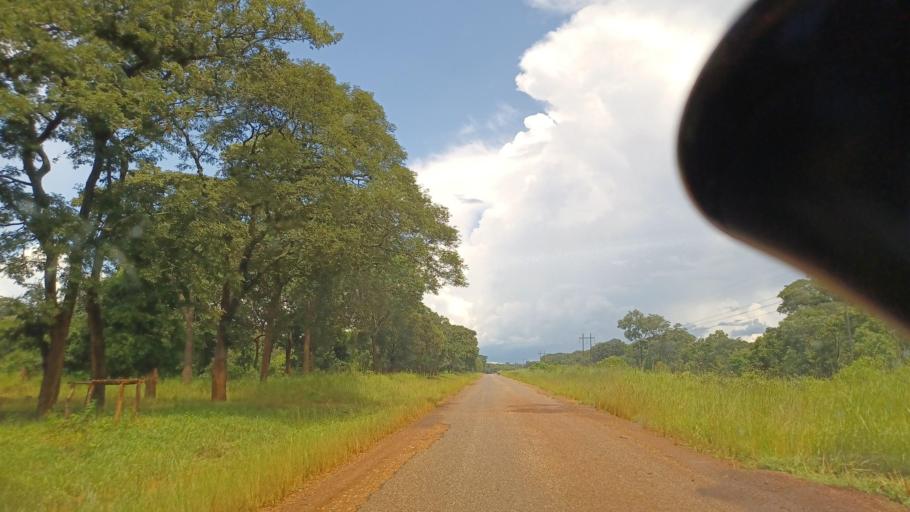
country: ZM
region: North-Western
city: Kasempa
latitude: -12.8999
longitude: 26.0551
